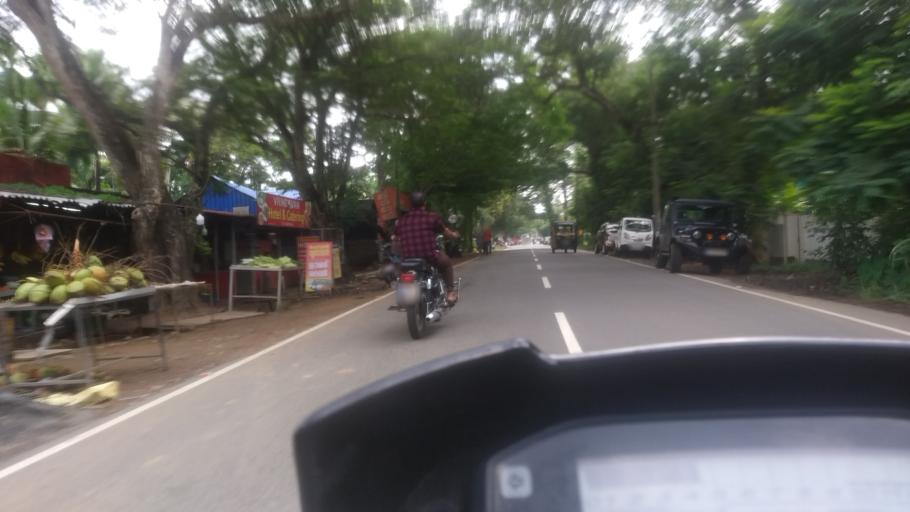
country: IN
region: Kerala
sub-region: Ernakulam
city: Elur
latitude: 10.1309
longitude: 76.2851
